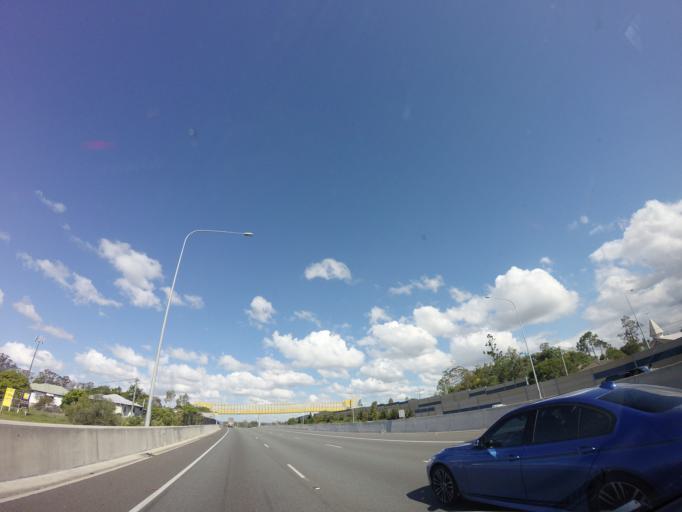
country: AU
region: Queensland
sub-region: Ipswich
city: Riverview
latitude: -27.5971
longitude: 152.8496
